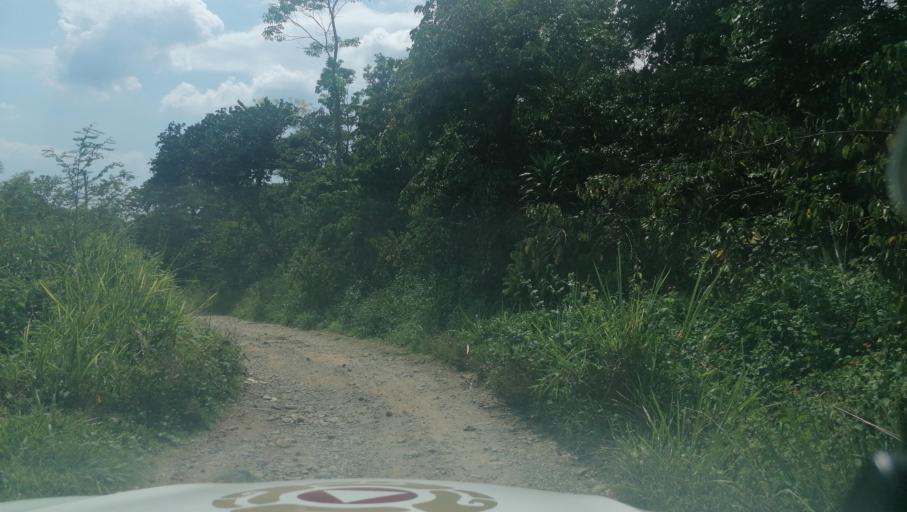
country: MX
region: Chiapas
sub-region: Cacahoatan
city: Benito Juarez
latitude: 15.0555
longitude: -92.2280
